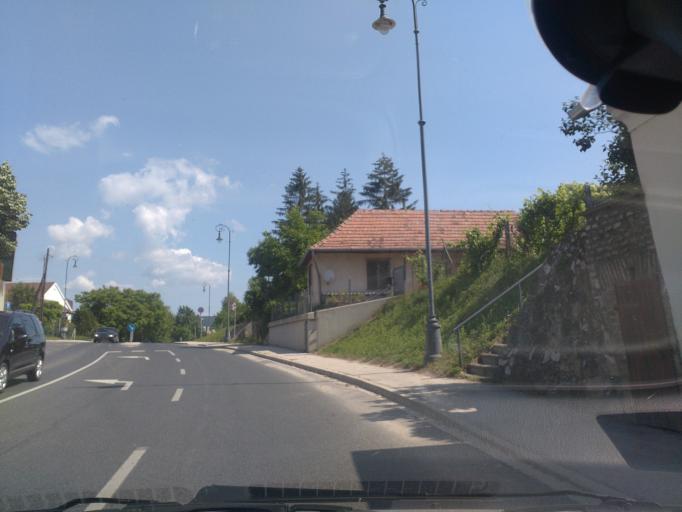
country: HU
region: Komarom-Esztergom
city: Esztergom
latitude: 47.7983
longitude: 18.7471
